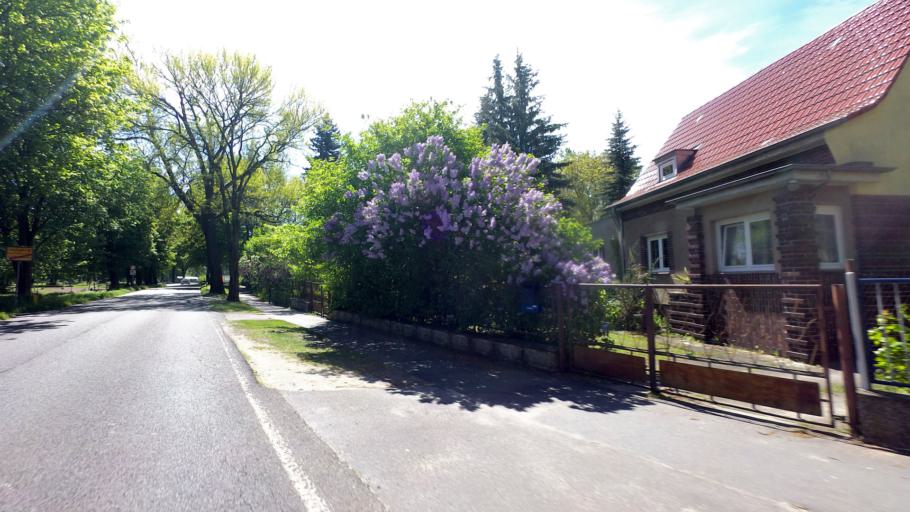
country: DE
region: Brandenburg
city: Luckenwalde
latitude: 52.0774
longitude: 13.1839
